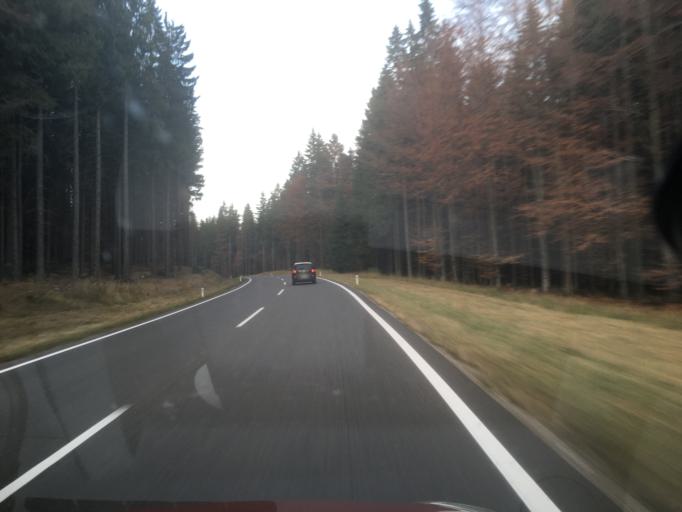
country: AT
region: Lower Austria
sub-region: Politischer Bezirk Zwettl
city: Langschlag
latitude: 48.5573
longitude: 14.7078
